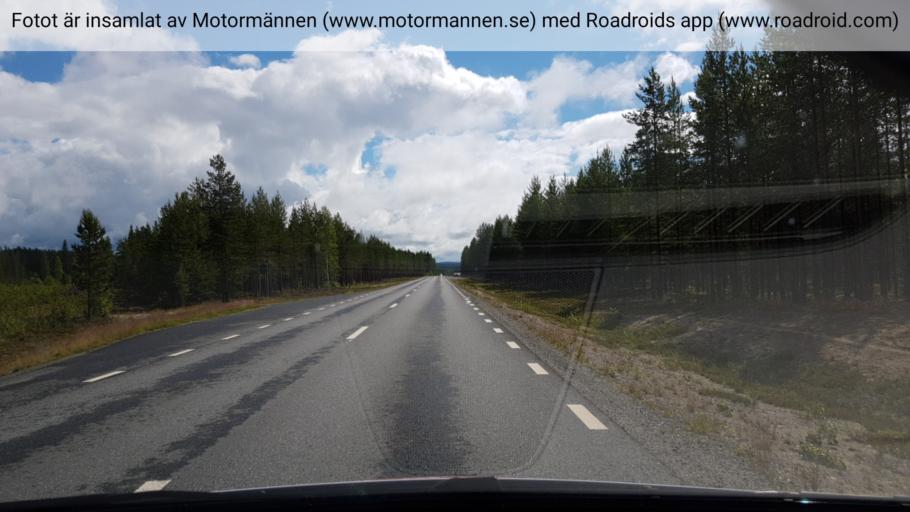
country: SE
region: Vaesterbotten
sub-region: Bjurholms Kommun
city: Bjurholm
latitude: 64.3142
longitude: 19.1610
